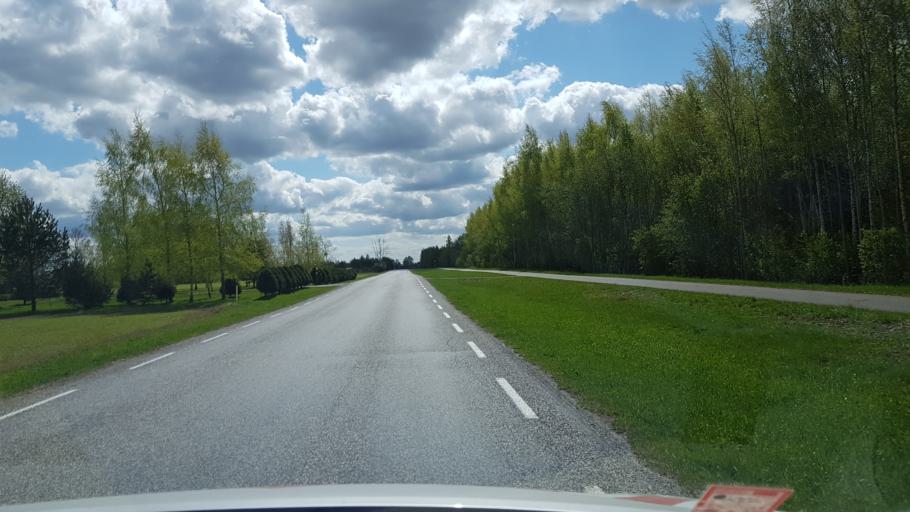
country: EE
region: Jogevamaa
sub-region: Poltsamaa linn
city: Poltsamaa
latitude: 58.6890
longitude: 25.9481
